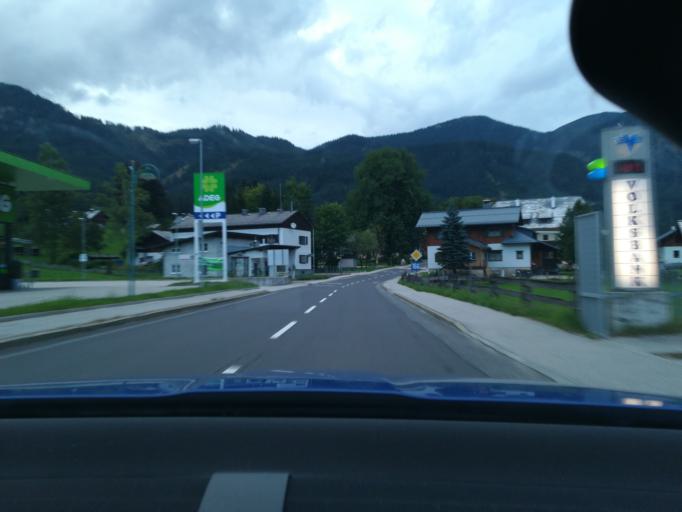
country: AT
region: Upper Austria
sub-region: Politischer Bezirk Gmunden
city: Bad Goisern
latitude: 47.5844
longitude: 13.5343
